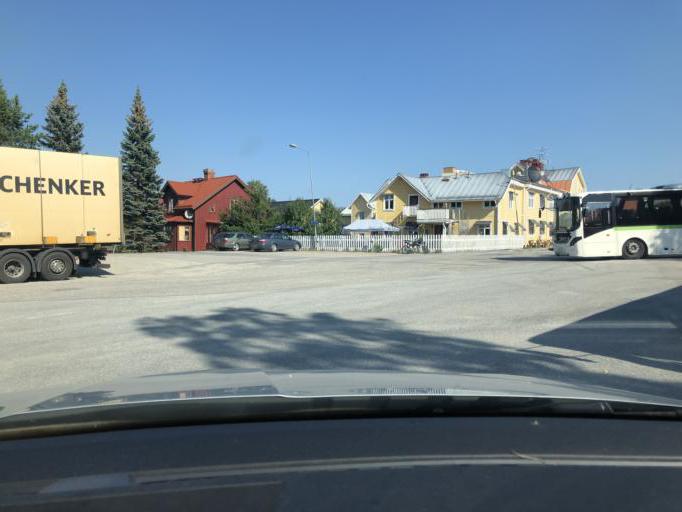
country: SE
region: Vaesternorrland
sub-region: OErnskoeldsviks Kommun
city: Bredbyn
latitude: 63.4488
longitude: 18.1060
